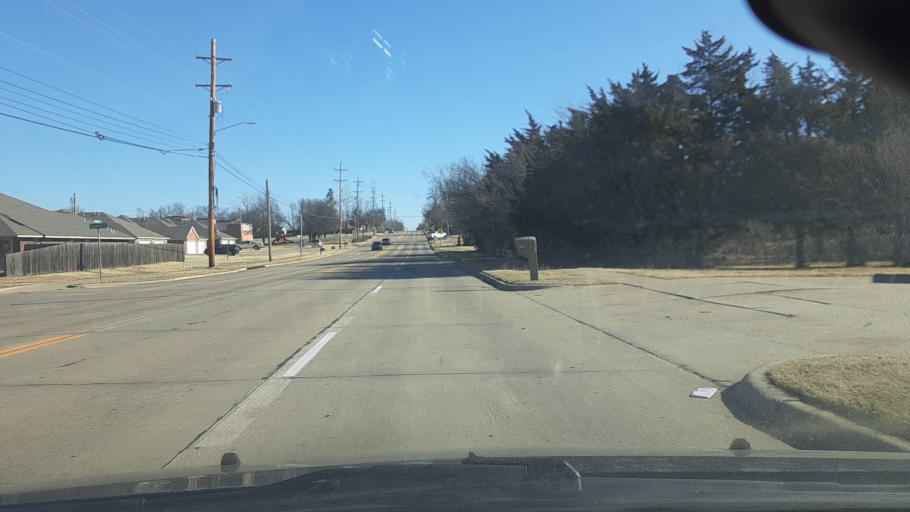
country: US
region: Oklahoma
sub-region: Kay County
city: Ponca City
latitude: 36.7384
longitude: -97.0581
